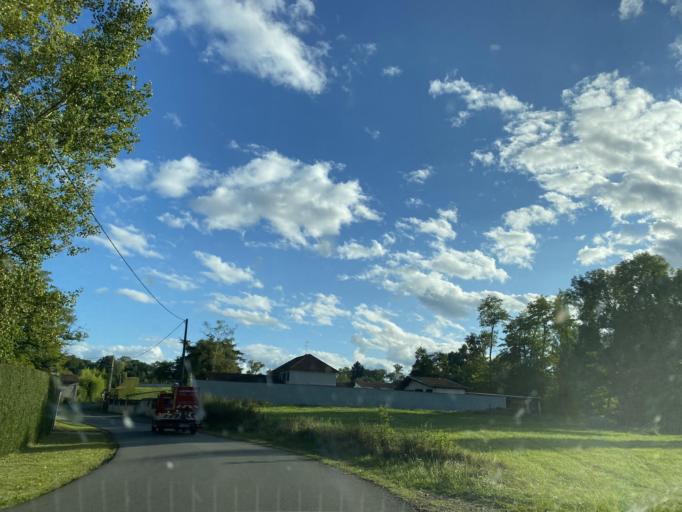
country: FR
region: Auvergne
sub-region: Departement du Puy-de-Dome
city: Saint-Sylvestre-Pragoulin
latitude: 45.9993
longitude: 3.4230
